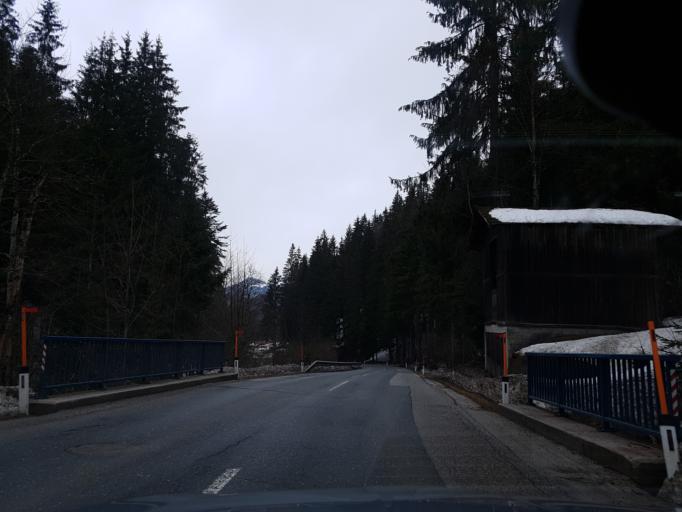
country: AT
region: Tyrol
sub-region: Politischer Bezirk Kufstein
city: Worgl
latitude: 47.4620
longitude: 12.0914
